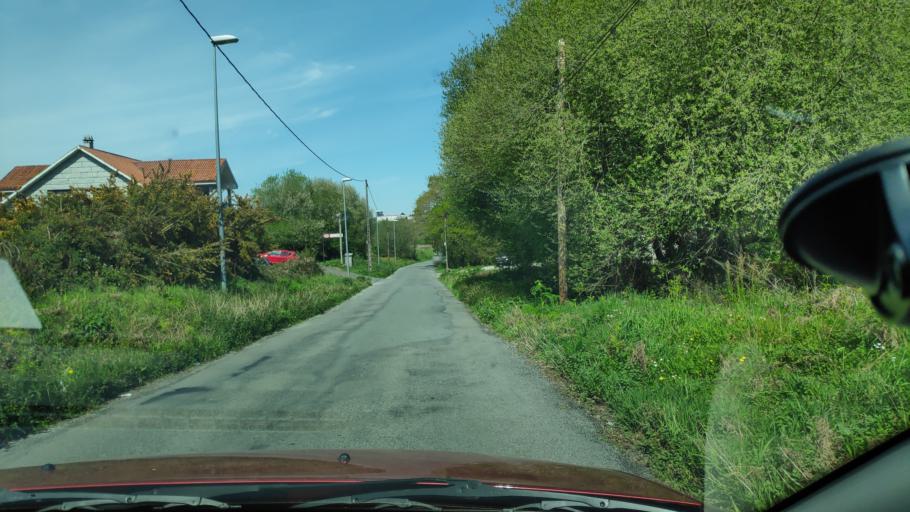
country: ES
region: Galicia
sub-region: Provincia da Coruna
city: Santiago de Compostela
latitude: 42.8928
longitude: -8.5255
